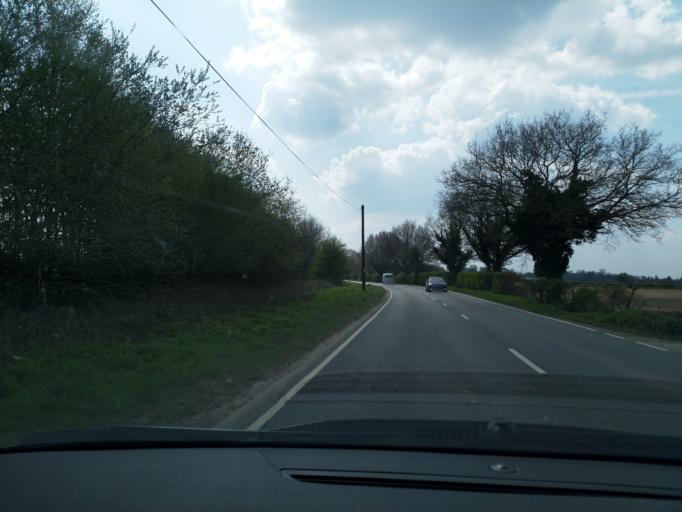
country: GB
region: England
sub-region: Warwickshire
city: Royal Leamington Spa
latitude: 52.3248
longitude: -1.5086
